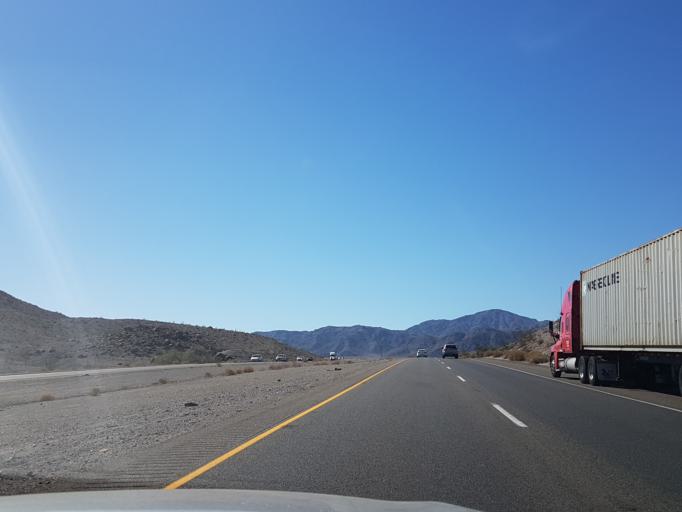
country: US
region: California
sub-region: San Bernardino County
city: Fort Irwin
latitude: 35.1953
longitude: -116.1466
